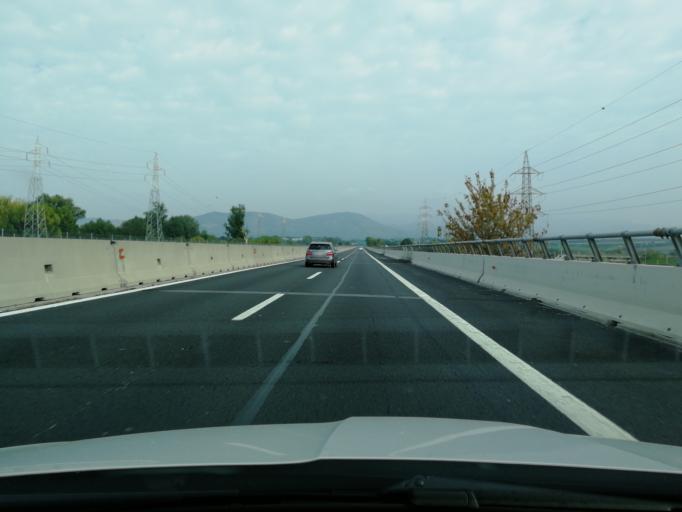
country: IT
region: Latium
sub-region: Citta metropolitana di Roma Capitale
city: Bagni di Tivoli
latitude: 41.9268
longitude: 12.7232
